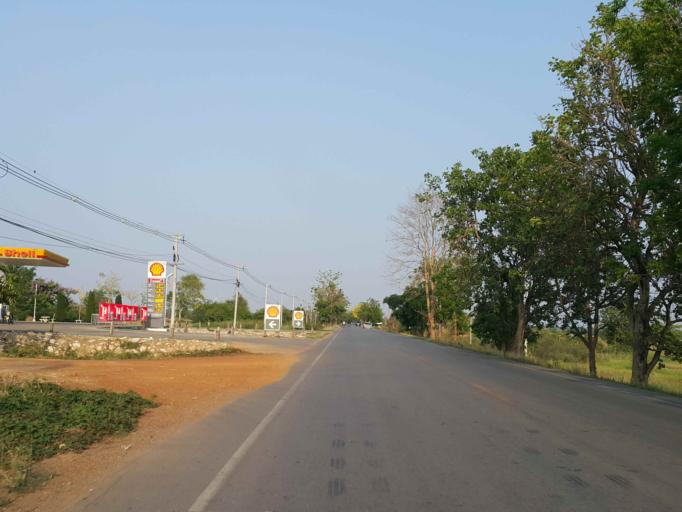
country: TH
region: Sukhothai
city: Sawankhalok
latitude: 17.3102
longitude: 99.8037
